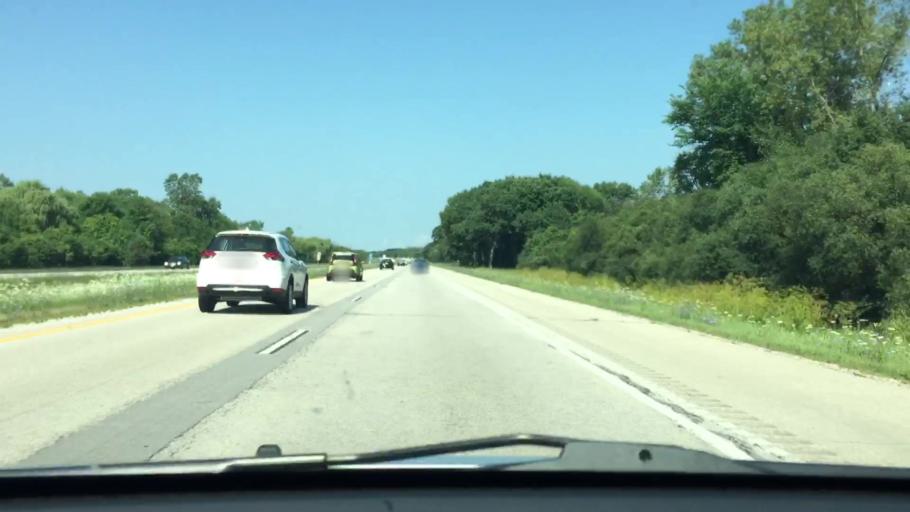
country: US
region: Wisconsin
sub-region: Waukesha County
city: Oconomowoc
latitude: 43.0697
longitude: -88.5046
